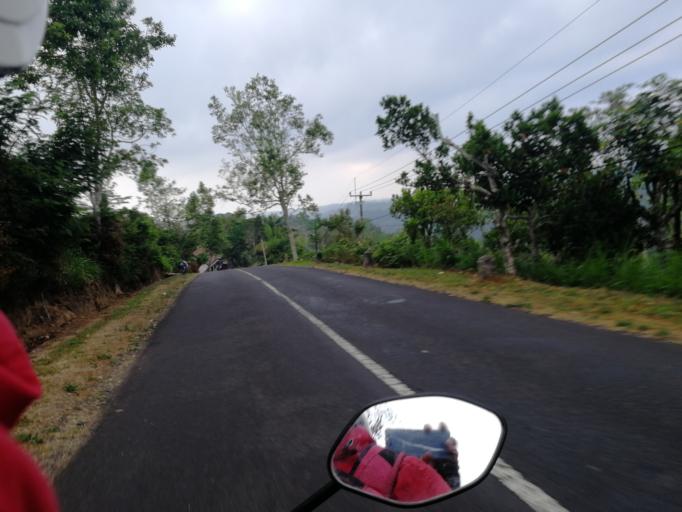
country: ID
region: Bali
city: Banjar Taro Kelod
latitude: -8.2554
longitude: 115.2453
